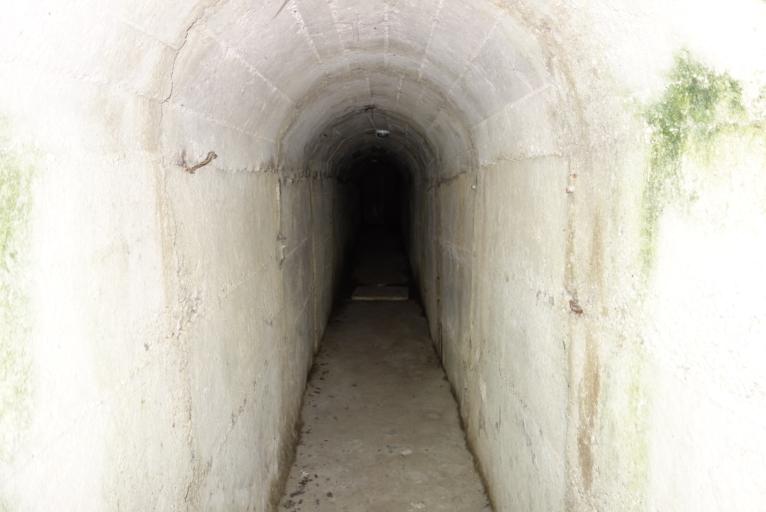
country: AL
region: Gjirokaster
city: Gjirokaster
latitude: 40.0746
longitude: 20.1403
